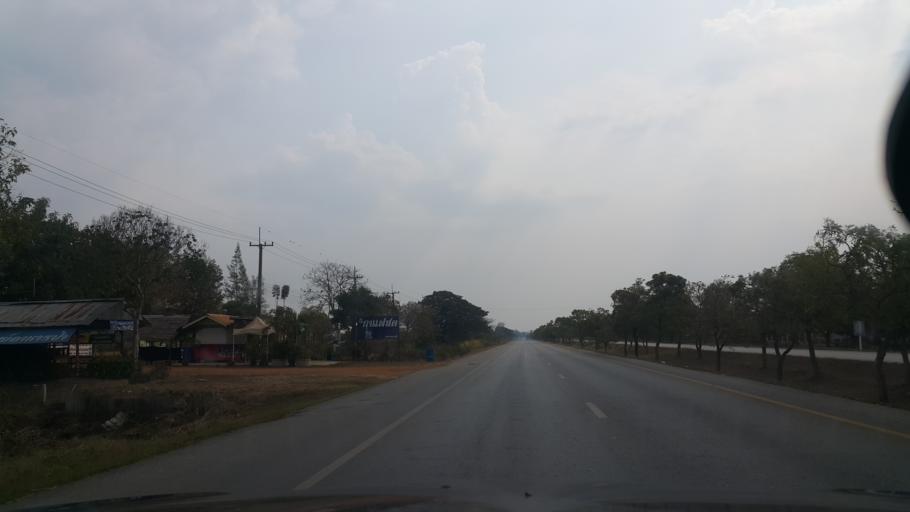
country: TH
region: Sukhothai
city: Sukhothai
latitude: 17.0626
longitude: 99.8830
